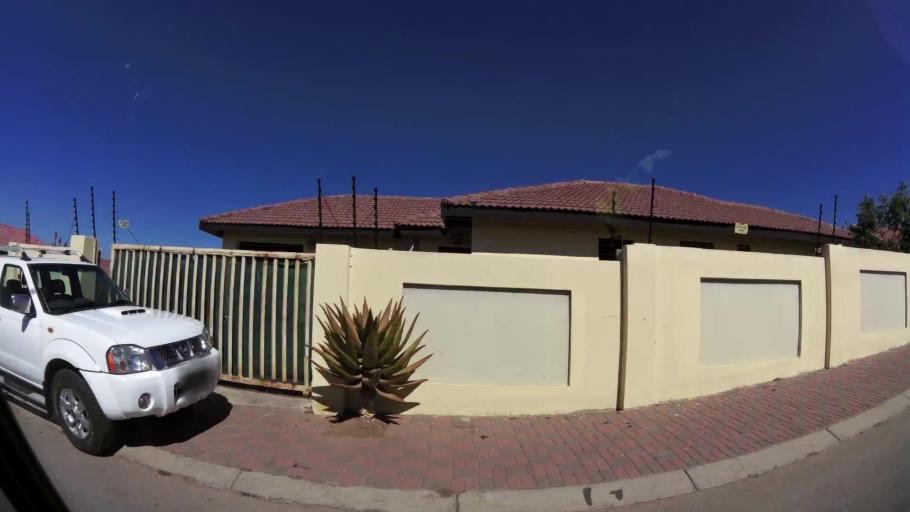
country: ZA
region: Limpopo
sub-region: Capricorn District Municipality
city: Polokwane
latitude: -23.8699
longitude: 29.4300
